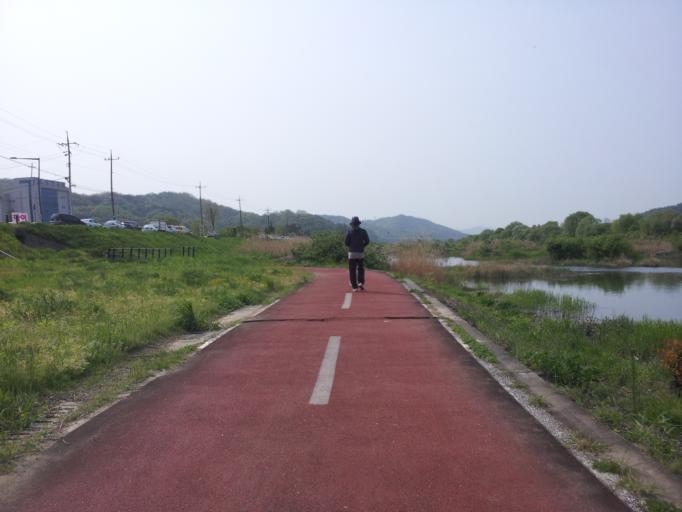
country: KR
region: Daejeon
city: Daejeon
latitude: 36.3474
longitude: 127.3509
